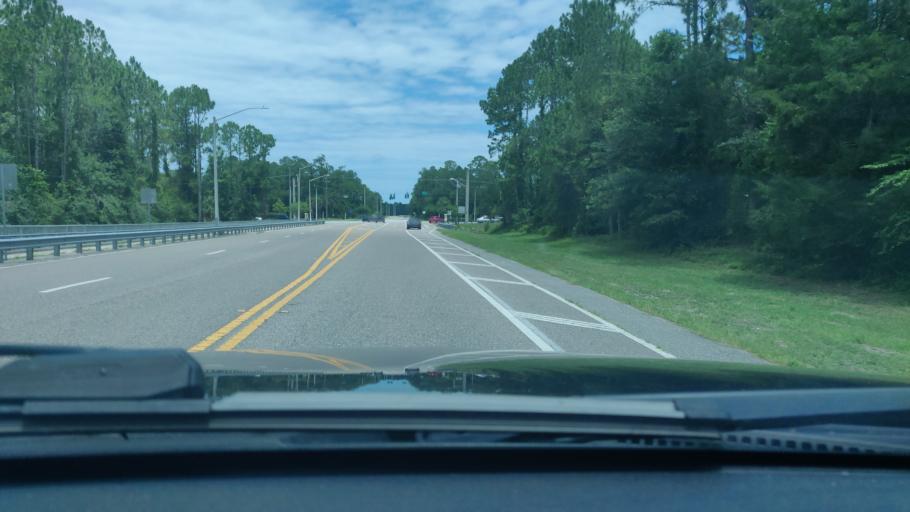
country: US
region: Florida
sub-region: Flagler County
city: Palm Coast
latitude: 29.5514
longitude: -81.2562
